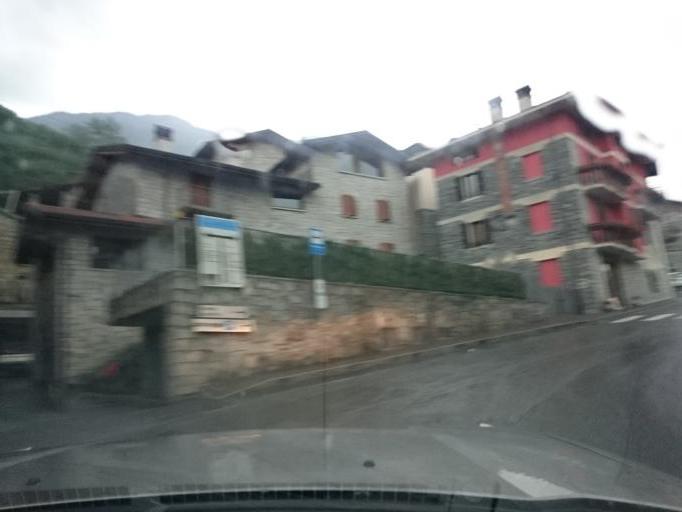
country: IT
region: Lombardy
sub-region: Provincia di Brescia
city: Ceto
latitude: 46.0105
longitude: 10.3522
